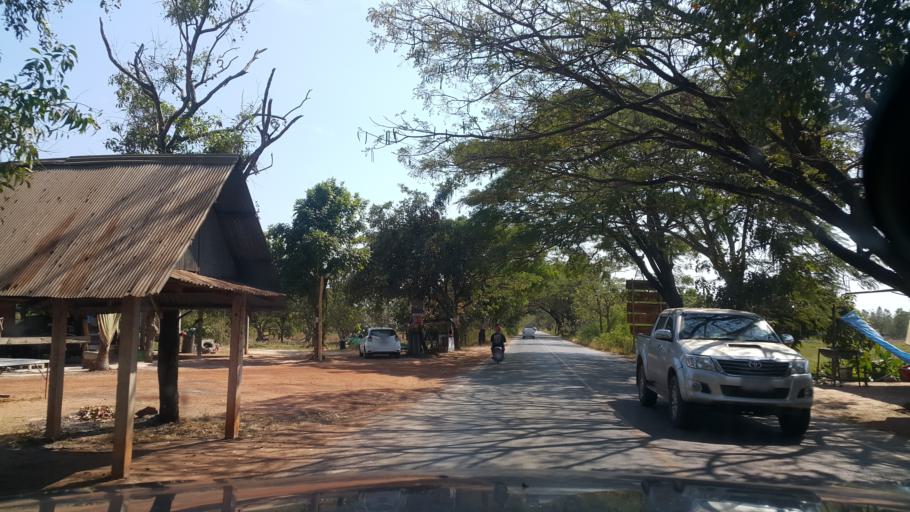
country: TH
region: Changwat Udon Thani
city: Udon Thani
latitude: 17.5064
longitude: 102.7601
